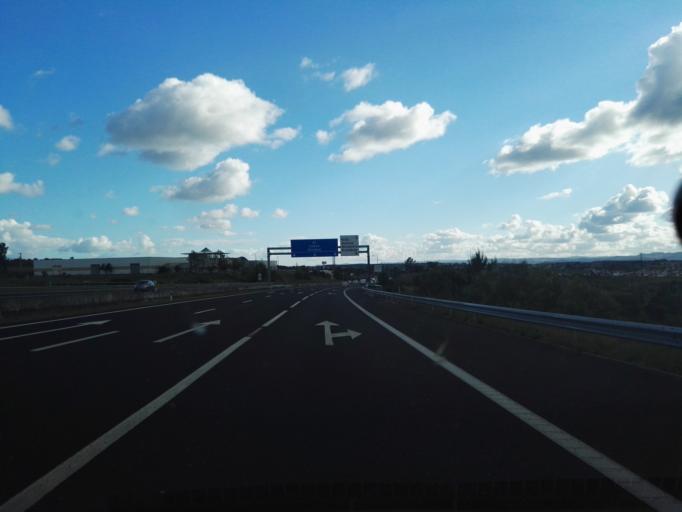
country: PT
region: Lisbon
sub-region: Azambuja
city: Aveiras de Cima
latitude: 39.1446
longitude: -8.8847
